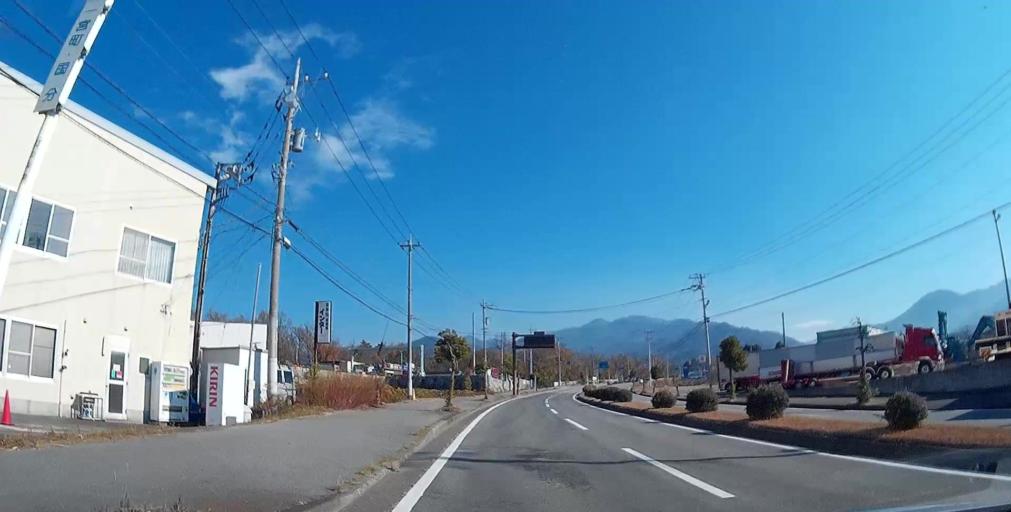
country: JP
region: Yamanashi
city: Isawa
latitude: 35.6322
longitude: 138.6782
